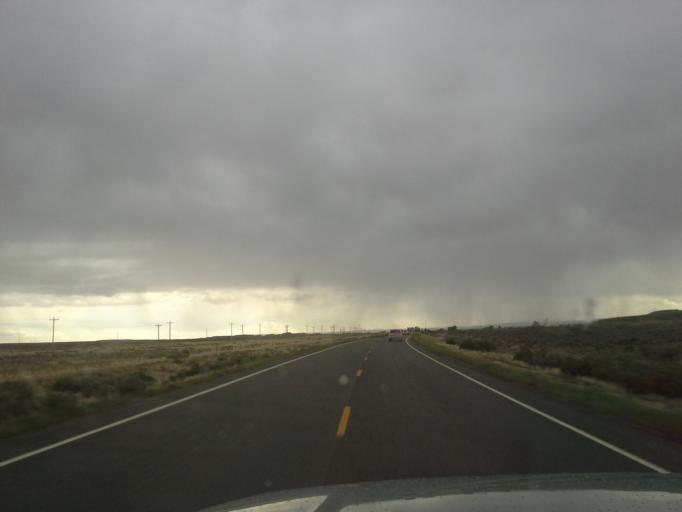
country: US
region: Wyoming
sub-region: Park County
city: Powell
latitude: 45.0224
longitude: -108.6311
